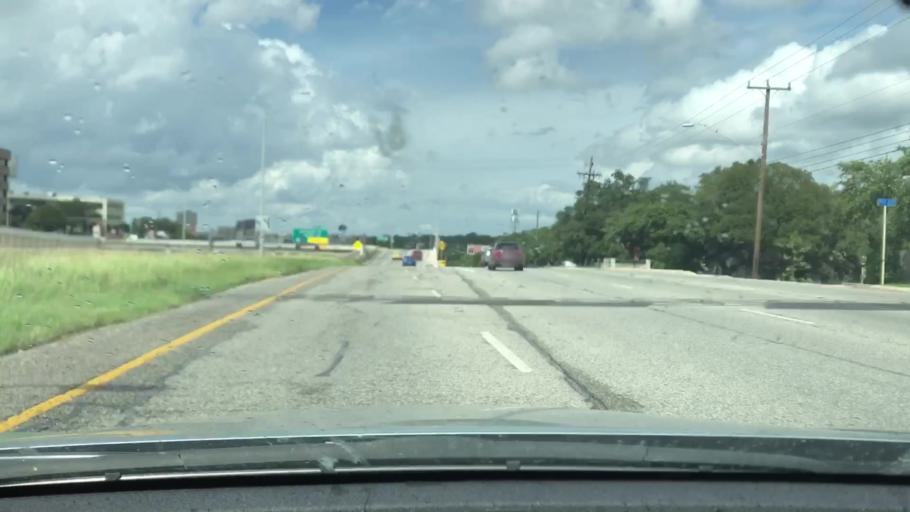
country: US
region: Texas
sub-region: Bexar County
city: Balcones Heights
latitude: 29.5210
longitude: -98.5547
